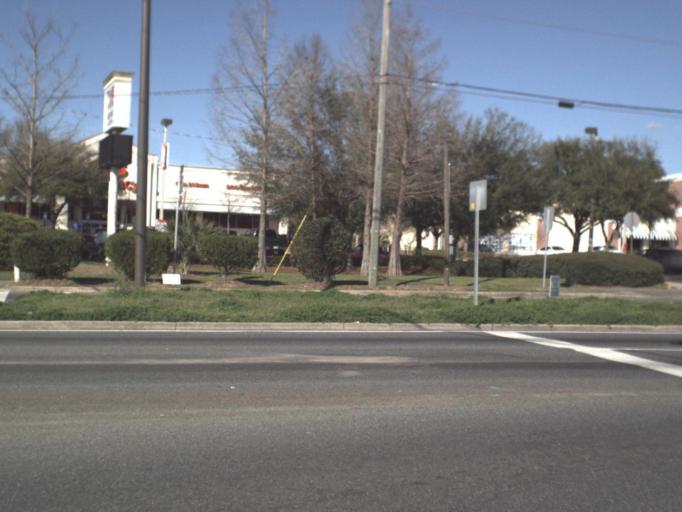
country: US
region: Florida
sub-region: Leon County
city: Tallahassee
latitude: 30.4368
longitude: -84.2617
